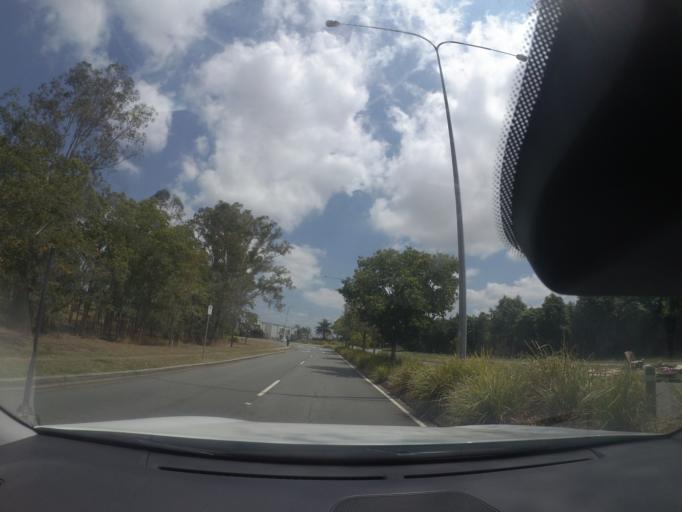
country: AU
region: Queensland
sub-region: Logan
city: Slacks Creek
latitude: -27.6642
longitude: 153.1440
